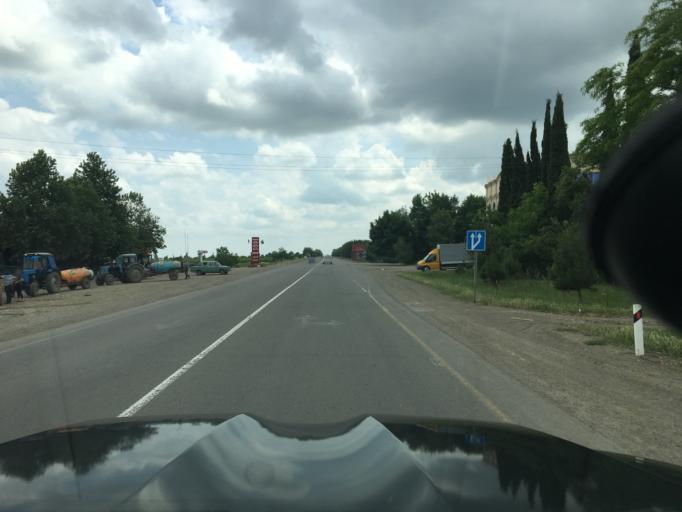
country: AZ
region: Tovuz
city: Tovuz
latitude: 40.9714
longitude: 45.6869
